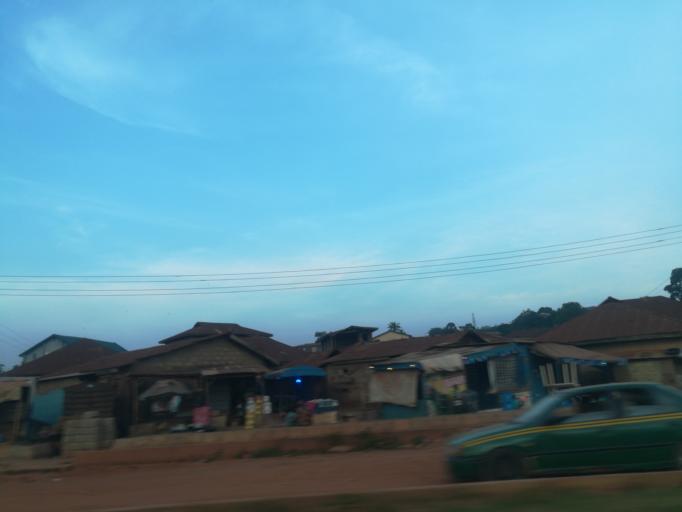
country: NG
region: Ogun
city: Abeokuta
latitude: 7.1758
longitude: 3.3545
